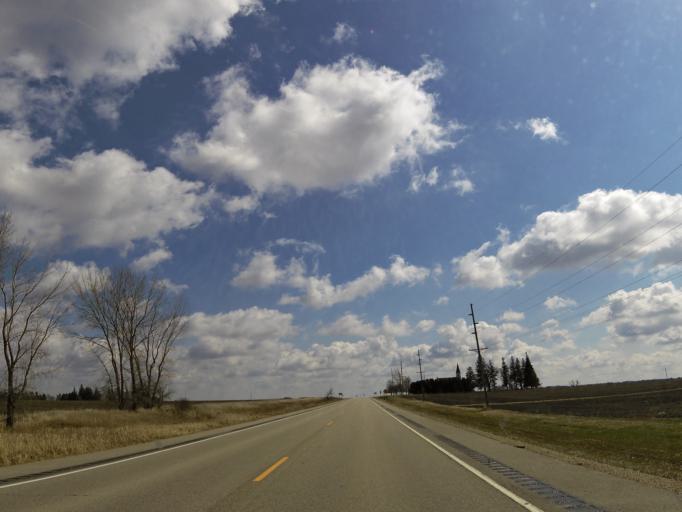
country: US
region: Minnesota
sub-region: Goodhue County
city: Kenyon
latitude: 44.2010
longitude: -92.9263
